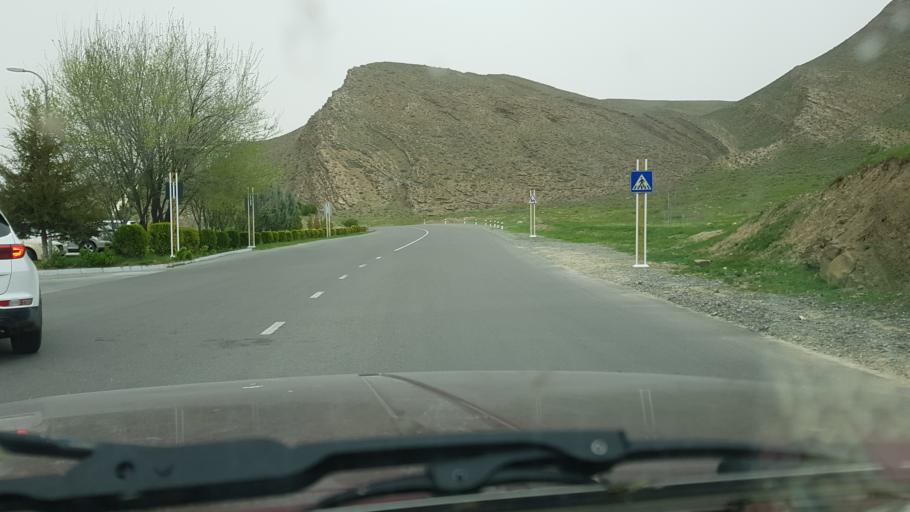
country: TM
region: Ahal
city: Arcabil
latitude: 38.0237
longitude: 58.0062
